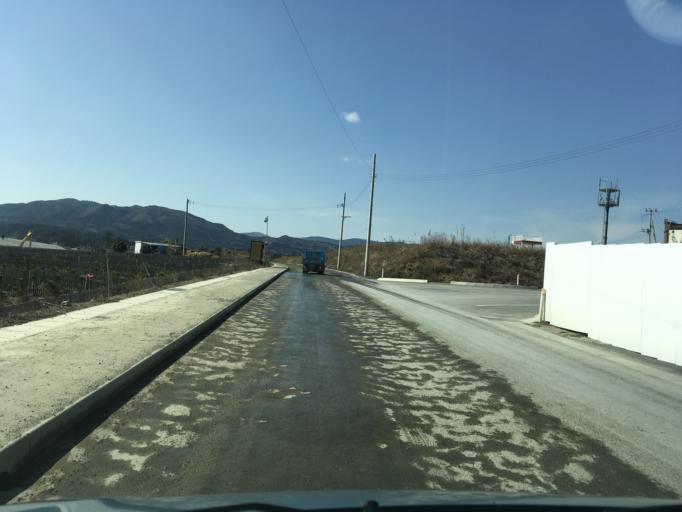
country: JP
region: Iwate
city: Ofunato
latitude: 38.8260
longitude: 141.5881
